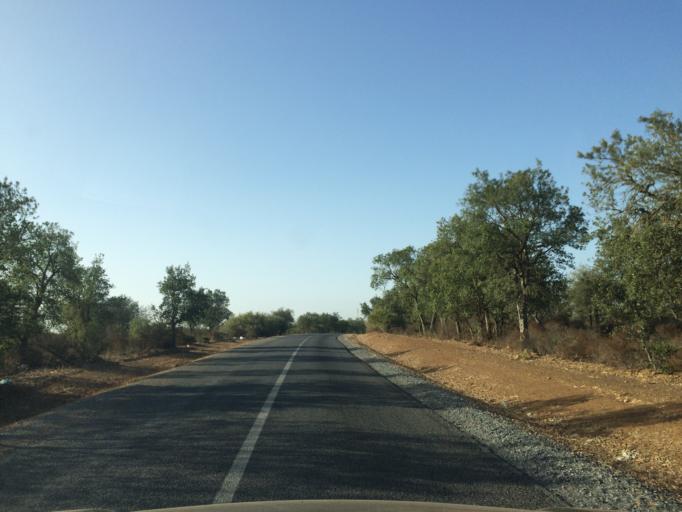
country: MA
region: Rabat-Sale-Zemmour-Zaer
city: Skhirat
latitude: 33.6514
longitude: -6.8816
